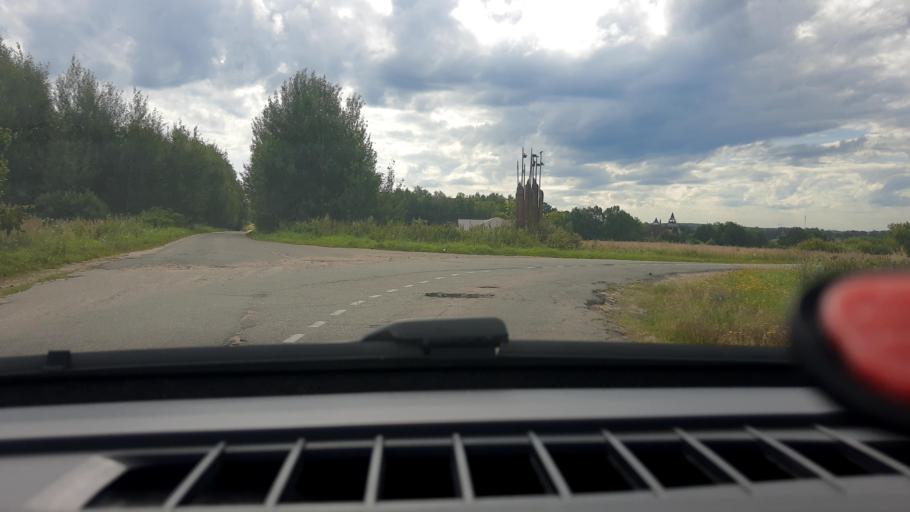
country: RU
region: Nizjnij Novgorod
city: Burevestnik
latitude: 56.0444
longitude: 43.7142
